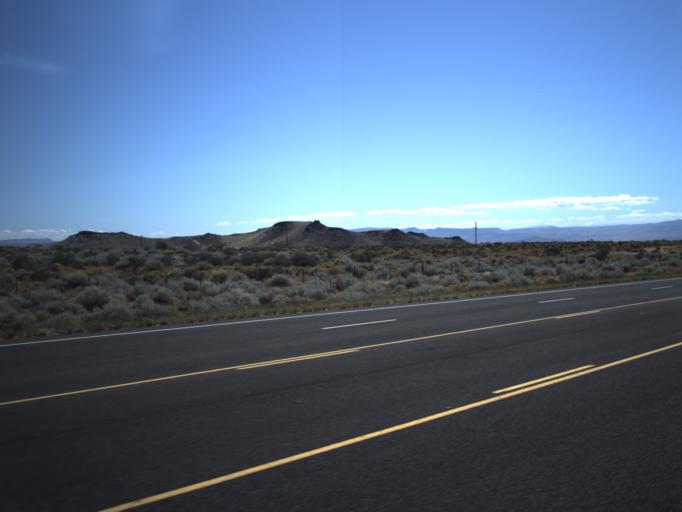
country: US
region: Utah
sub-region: Washington County
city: Santa Clara
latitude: 37.1844
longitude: -113.6194
